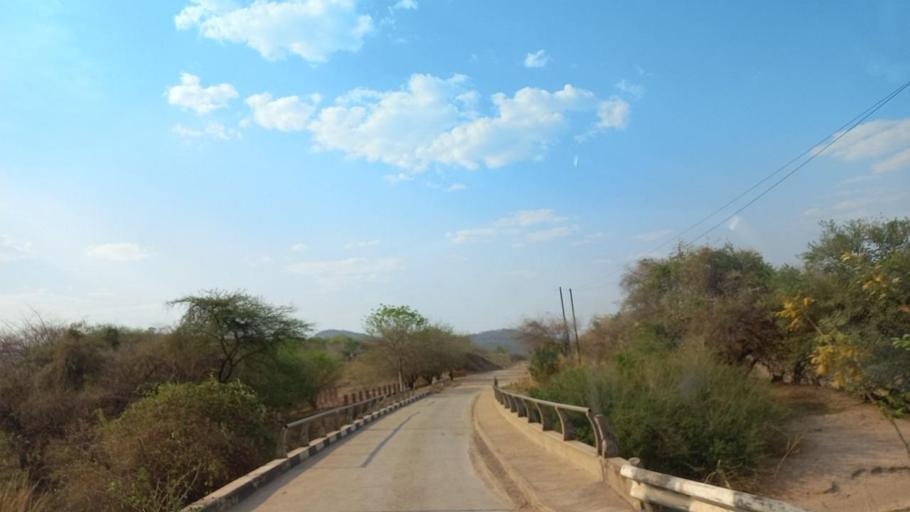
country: ZM
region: Lusaka
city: Luangwa
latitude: -14.9962
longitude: 30.2139
